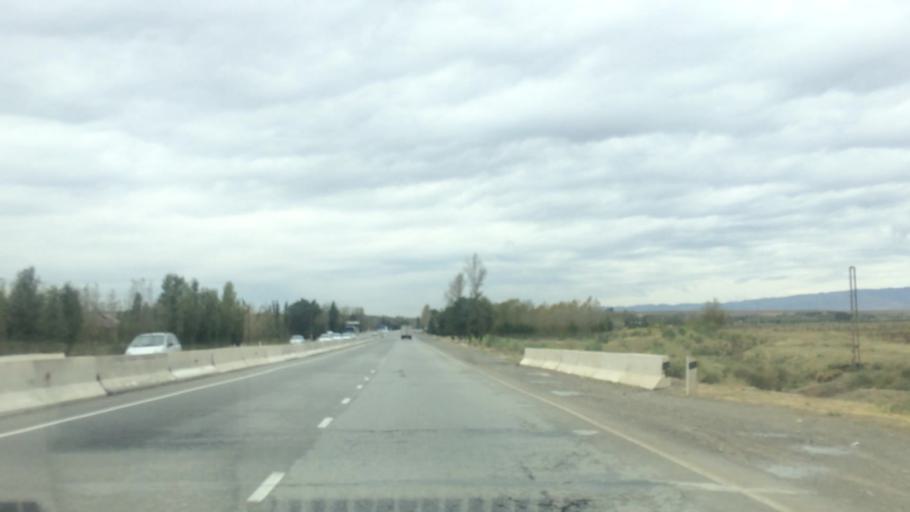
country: UZ
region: Jizzax
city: Jizzax
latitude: 39.9653
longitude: 67.5515
